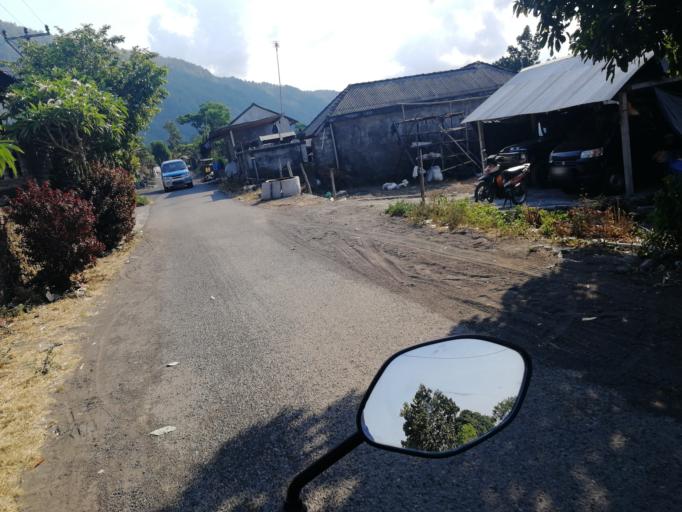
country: ID
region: Bali
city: Banjar Trunyan
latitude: -8.2746
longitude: 115.4142
